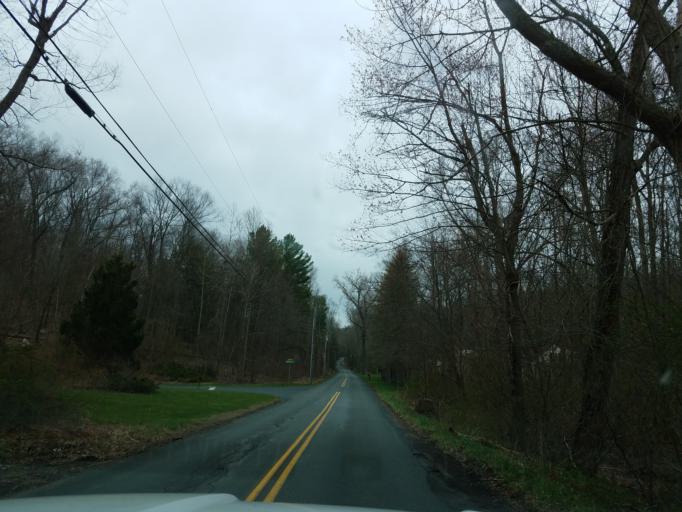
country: US
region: Connecticut
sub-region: Tolland County
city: Somers
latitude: 41.9815
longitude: -72.4228
